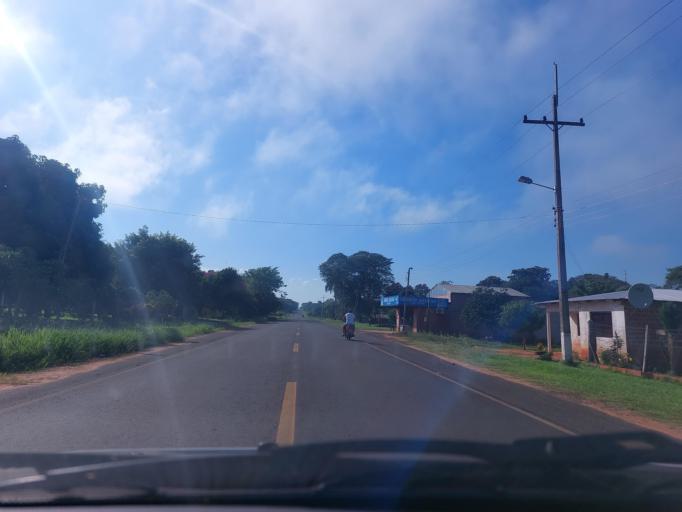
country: PY
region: San Pedro
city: Guayaybi
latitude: -24.5320
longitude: -56.5135
